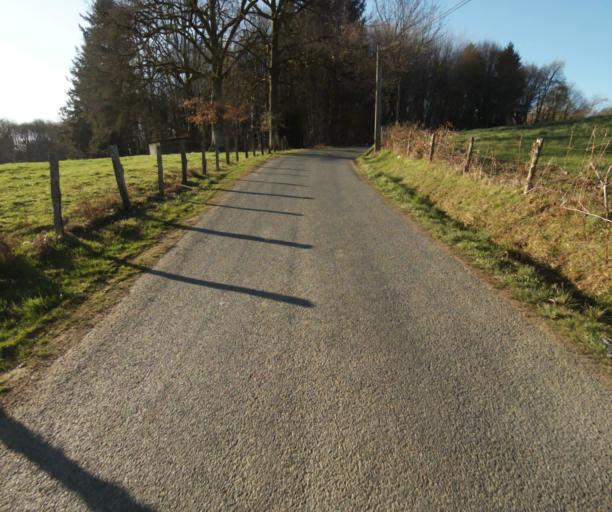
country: FR
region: Limousin
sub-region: Departement de la Correze
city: Seilhac
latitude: 45.3594
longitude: 1.7338
